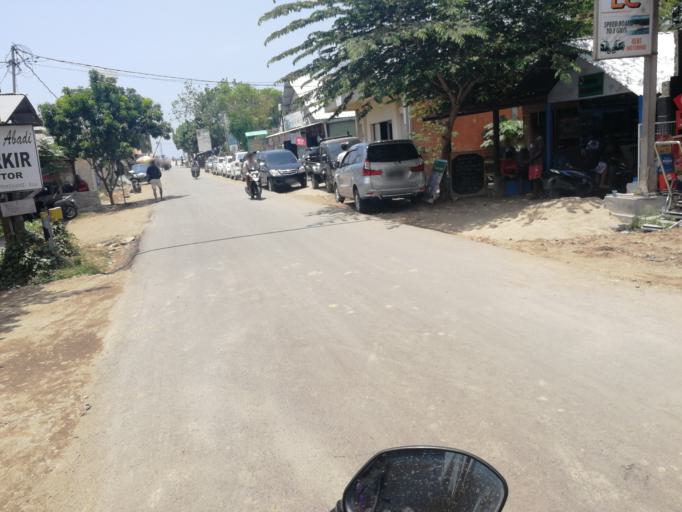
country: ID
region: West Nusa Tenggara
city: Pemenang
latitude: -8.3950
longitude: 116.0998
